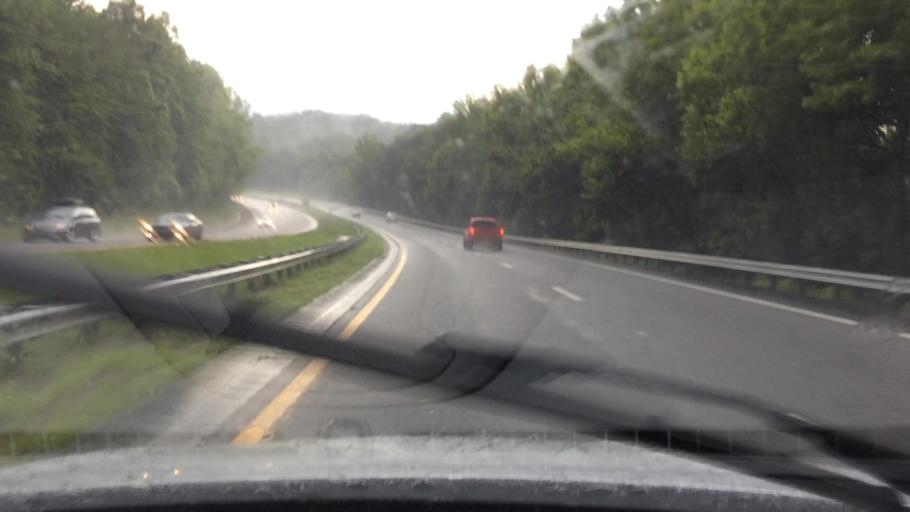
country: US
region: South Carolina
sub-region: Spartanburg County
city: Landrum
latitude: 35.2125
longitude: -82.1831
